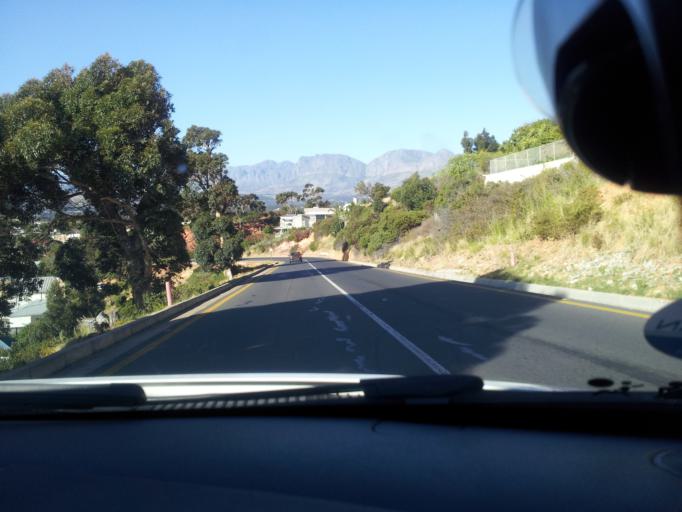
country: ZA
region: Western Cape
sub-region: Overberg District Municipality
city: Grabouw
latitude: -34.1612
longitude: 18.8708
